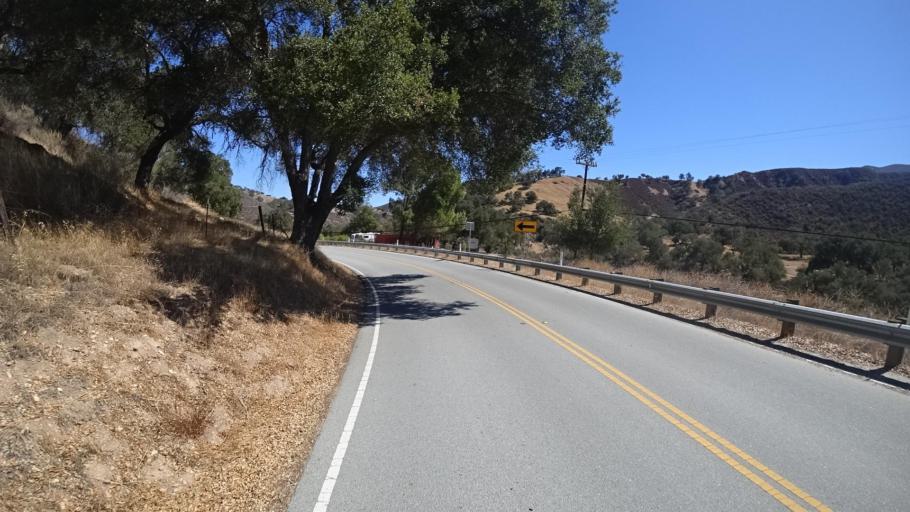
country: US
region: California
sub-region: Monterey County
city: Greenfield
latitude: 36.2375
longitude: -121.4461
